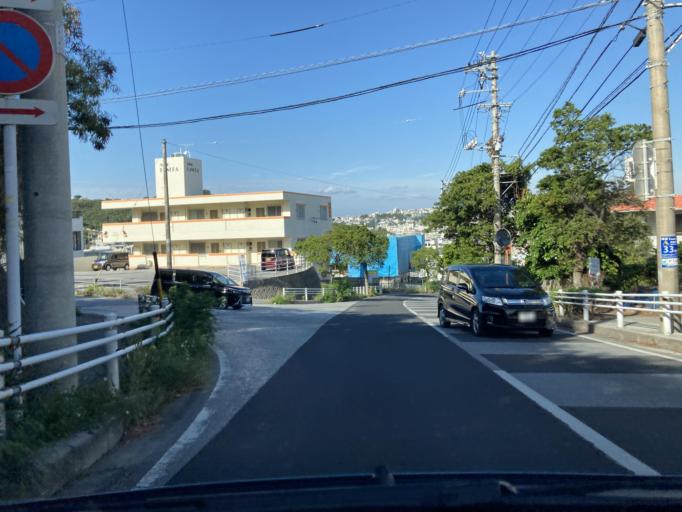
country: JP
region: Okinawa
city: Tomigusuku
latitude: 26.1788
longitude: 127.7062
